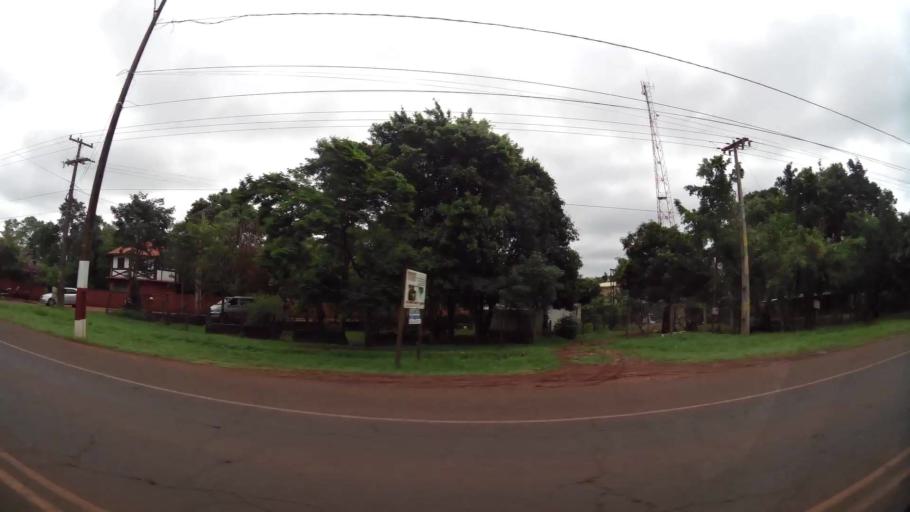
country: PY
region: Alto Parana
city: Ciudad del Este
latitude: -25.4224
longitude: -54.6371
